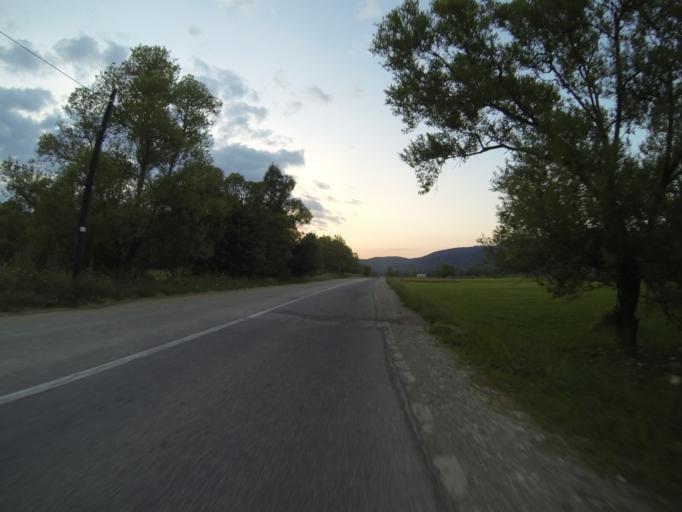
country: RO
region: Brasov
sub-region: Comuna Sinca Noua
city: Sinca Noua
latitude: 45.7162
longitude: 25.2410
